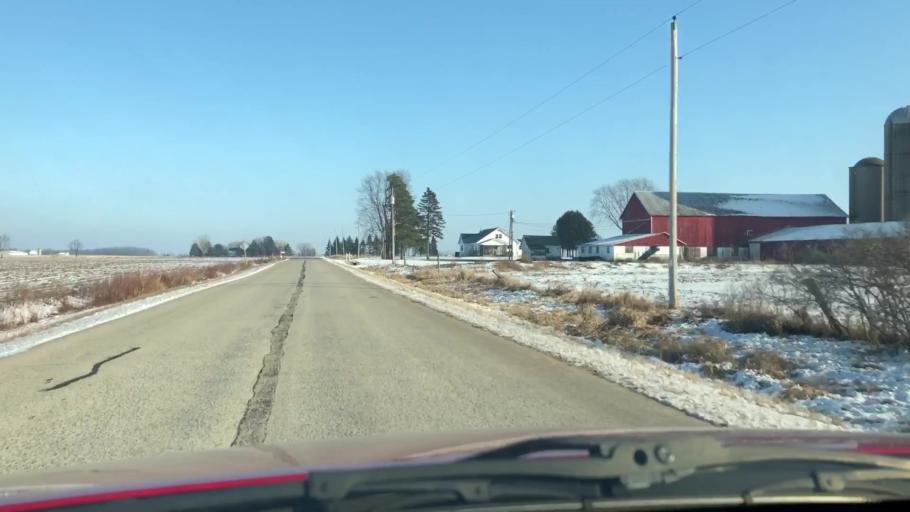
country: US
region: Wisconsin
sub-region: Outagamie County
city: Seymour
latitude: 44.4870
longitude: -88.3254
